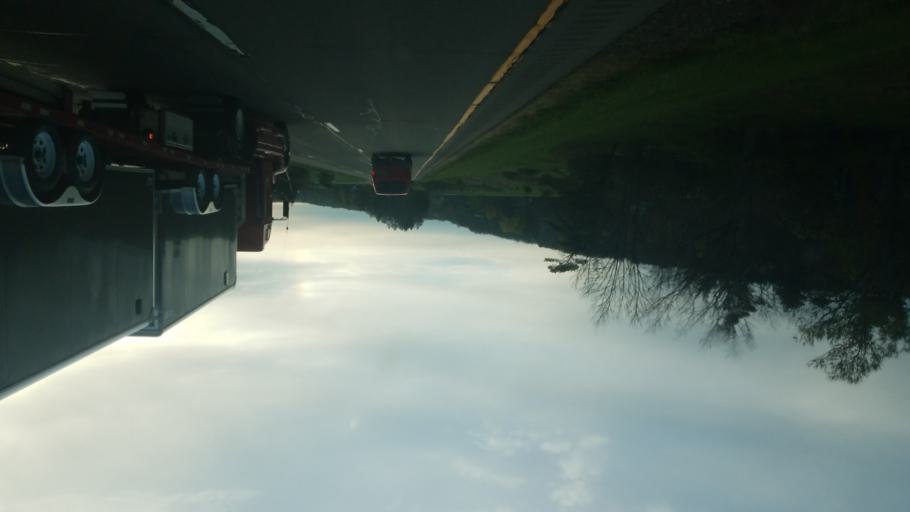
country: US
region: New York
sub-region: Allegany County
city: Friendship
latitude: 42.2139
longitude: -78.1415
